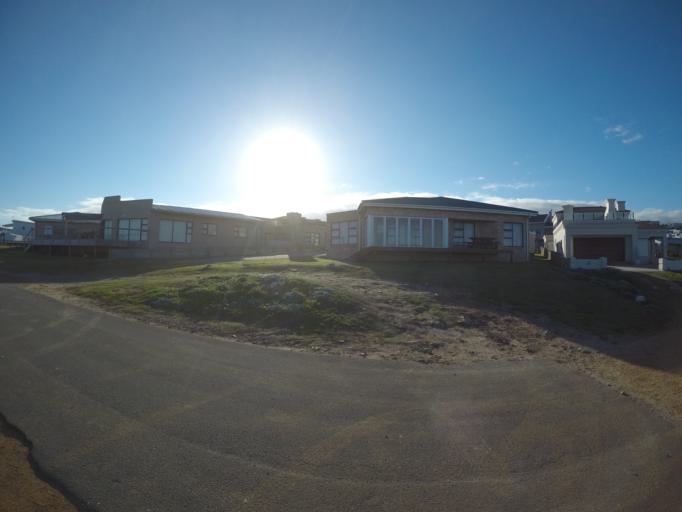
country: ZA
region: Western Cape
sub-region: Eden District Municipality
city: Riversdale
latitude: -34.4254
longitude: 21.3448
